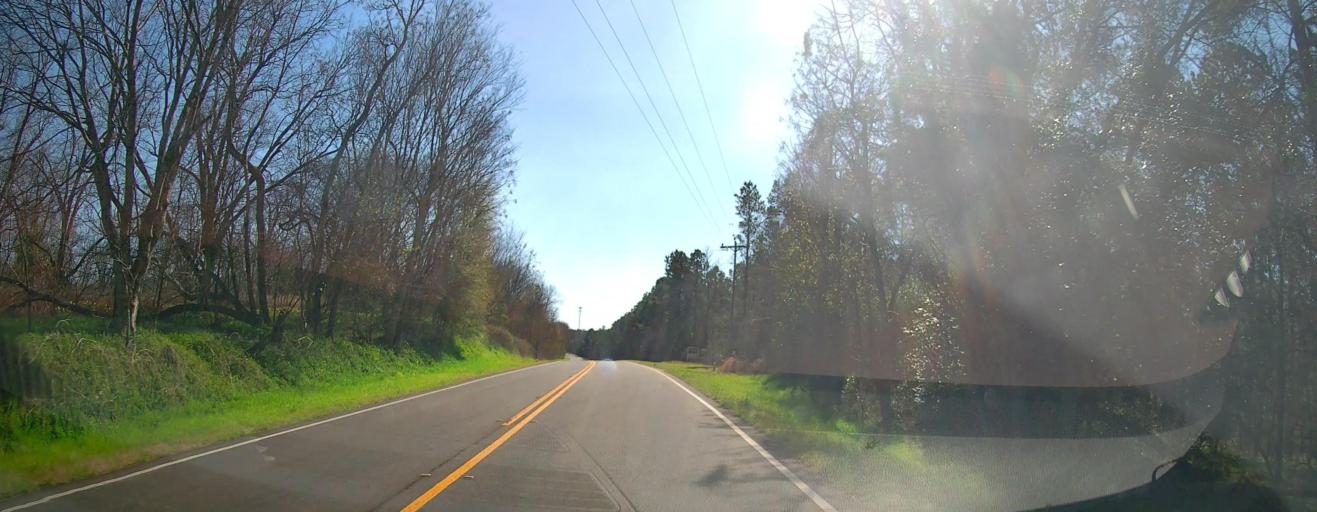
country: US
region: Georgia
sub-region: Macon County
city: Montezuma
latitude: 32.3559
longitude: -84.0168
